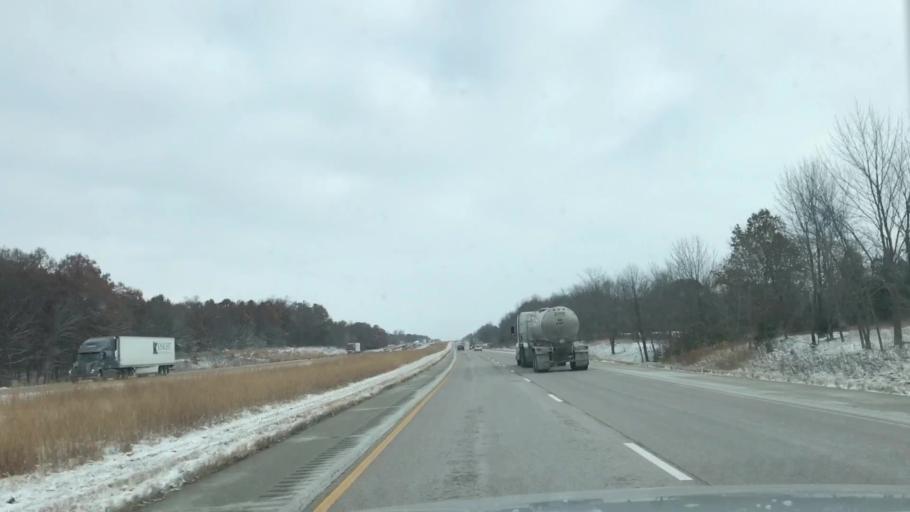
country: US
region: Illinois
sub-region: Macoupin County
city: Mount Olive
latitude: 39.0987
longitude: -89.7355
